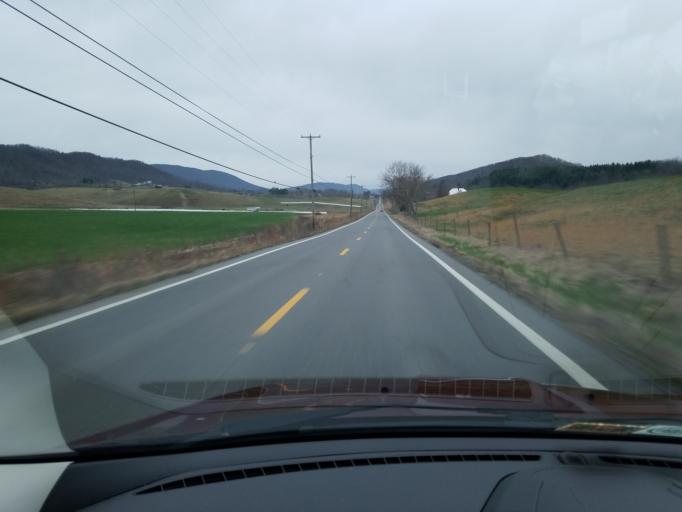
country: US
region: Virginia
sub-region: Giles County
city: Pearisburg
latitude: 37.4227
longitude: -80.7337
